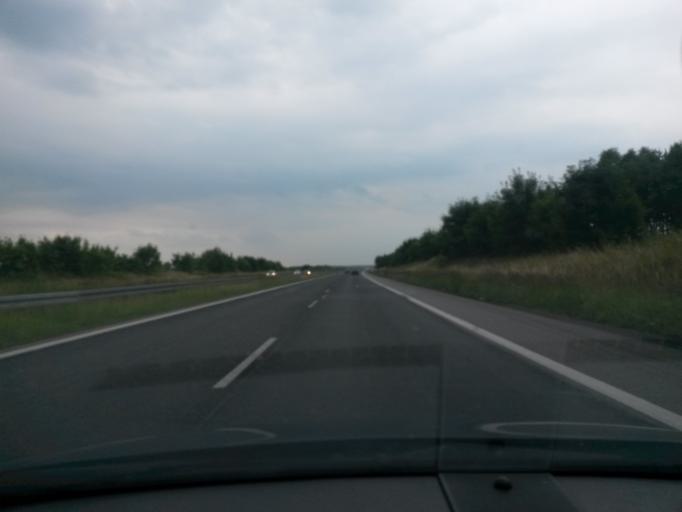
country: PL
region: Silesian Voivodeship
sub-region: Powiat czestochowski
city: Mykanow
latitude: 50.9218
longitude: 19.2219
